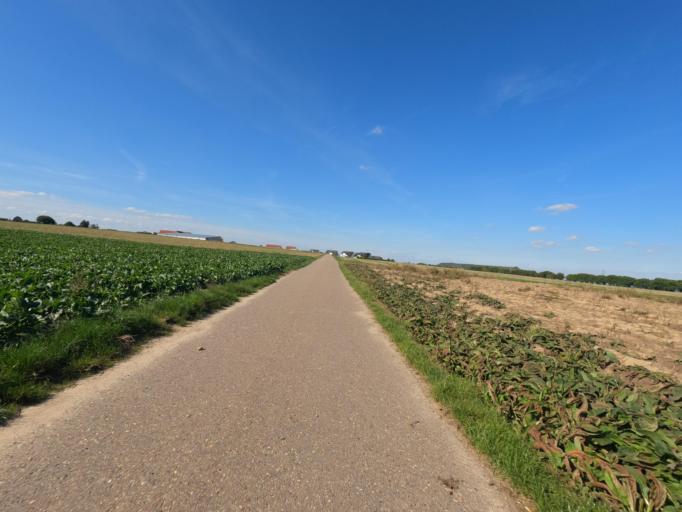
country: DE
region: North Rhine-Westphalia
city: Siersdorf
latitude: 50.8974
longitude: 6.2375
